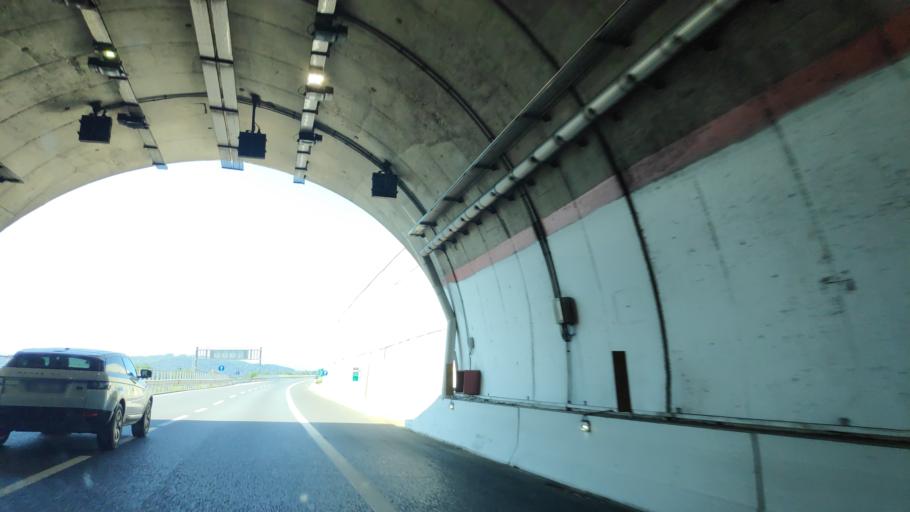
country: IT
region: Calabria
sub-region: Provincia di Reggio Calabria
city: Seminara
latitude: 38.3533
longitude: 15.8688
